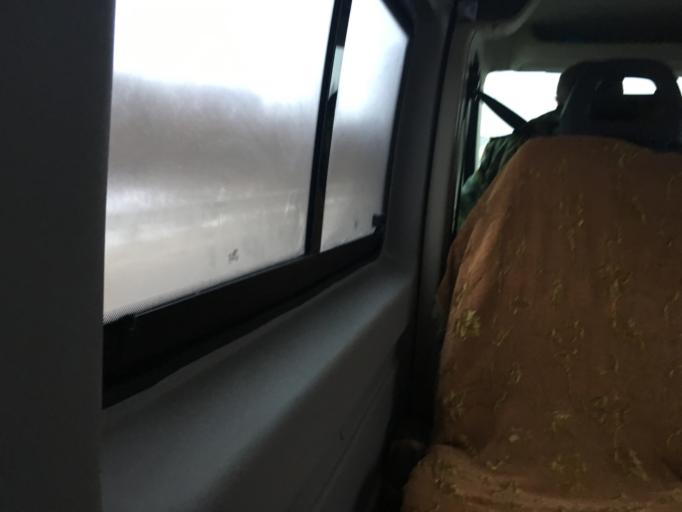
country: RU
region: Tula
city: Dubna
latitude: 54.0641
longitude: 37.0382
